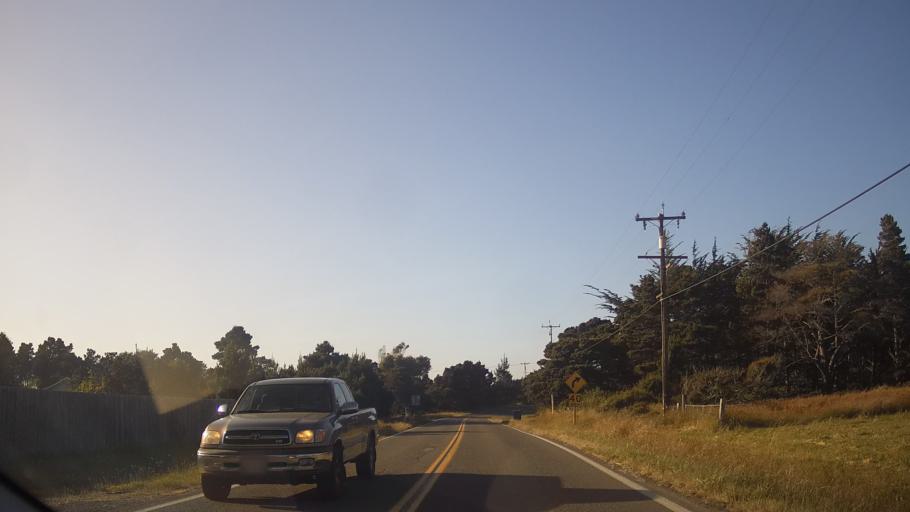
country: US
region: California
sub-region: Mendocino County
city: Fort Bragg
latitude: 39.4755
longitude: -123.7978
